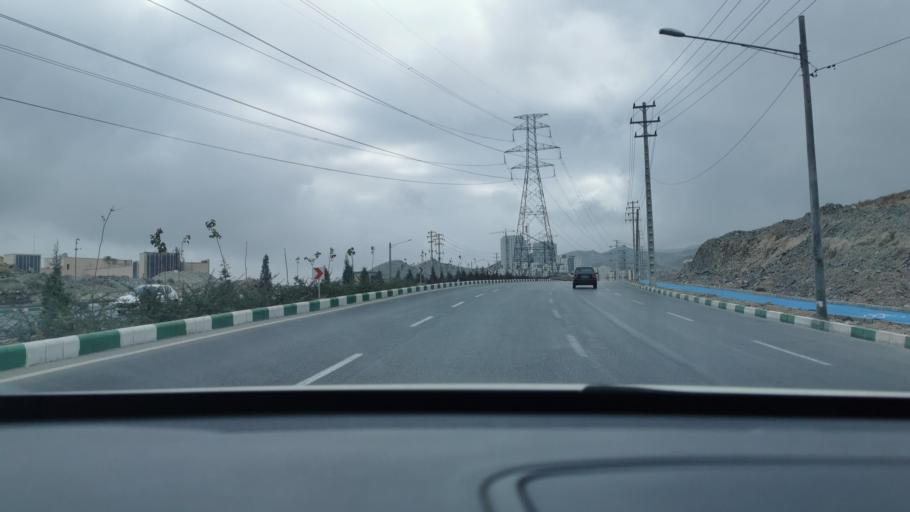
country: IR
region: Razavi Khorasan
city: Mashhad
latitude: 36.2780
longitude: 59.5356
